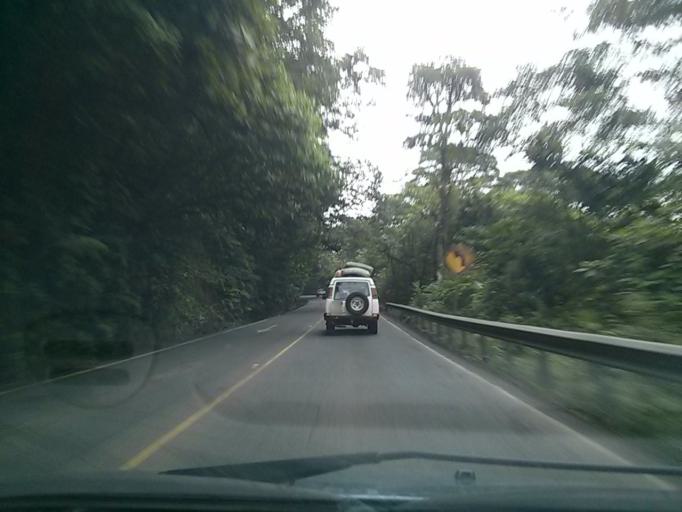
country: CR
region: San Jose
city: Dulce Nombre de Jesus
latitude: 10.1149
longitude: -83.9731
